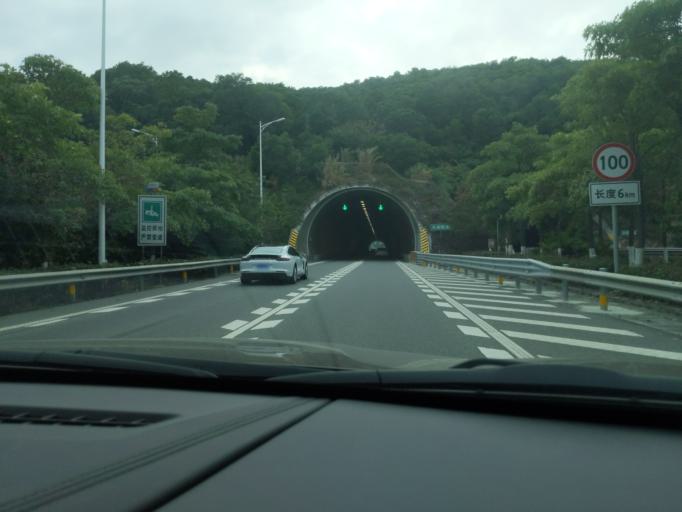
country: CN
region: Fujian
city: Dongshi
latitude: 24.7028
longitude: 118.3794
